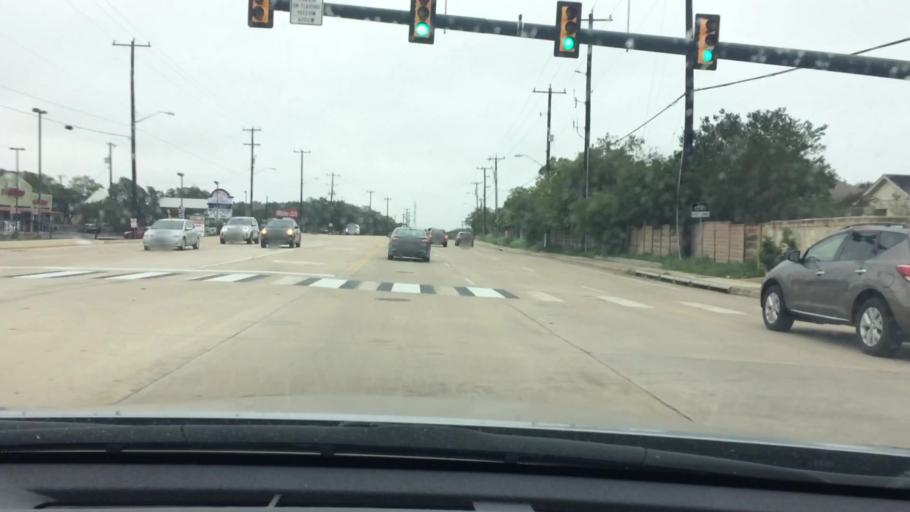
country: US
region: Texas
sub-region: Bexar County
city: Hollywood Park
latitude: 29.6439
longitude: -98.4250
